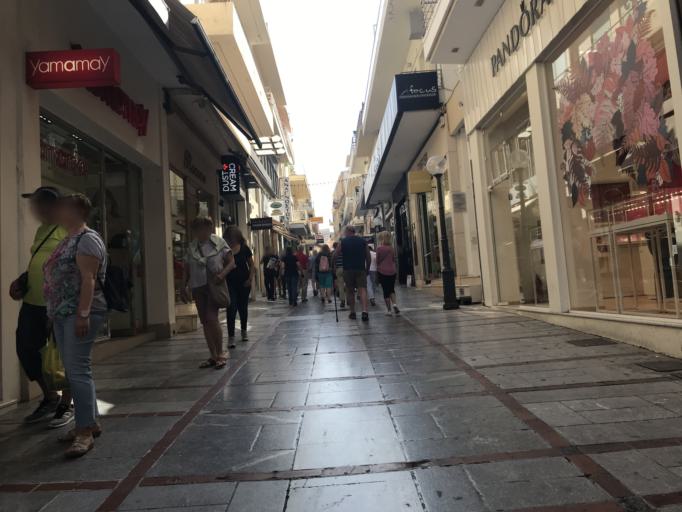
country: GR
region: Crete
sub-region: Nomos Irakleiou
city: Irakleion
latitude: 35.3390
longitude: 25.1335
